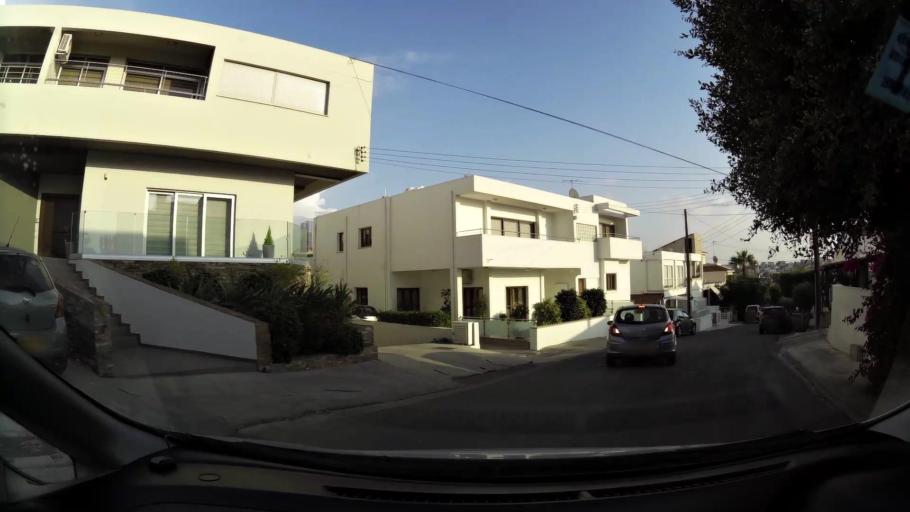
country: CY
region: Lefkosia
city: Nicosia
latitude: 35.1631
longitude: 33.3924
